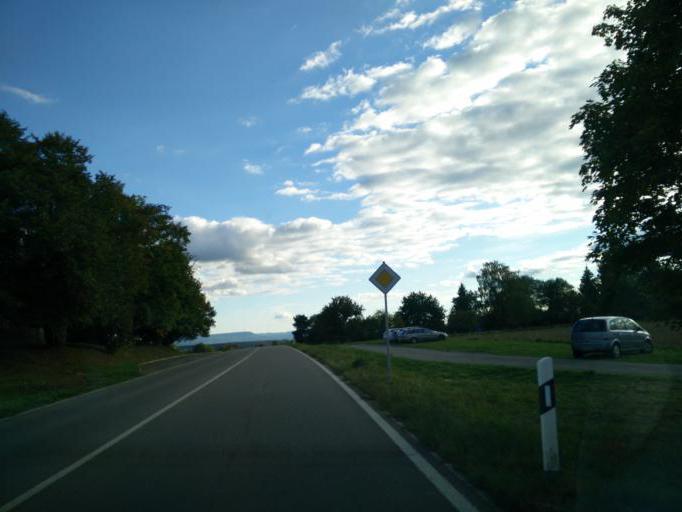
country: DE
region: Baden-Wuerttemberg
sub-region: Tuebingen Region
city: Kusterdingen
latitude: 48.5523
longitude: 9.0953
